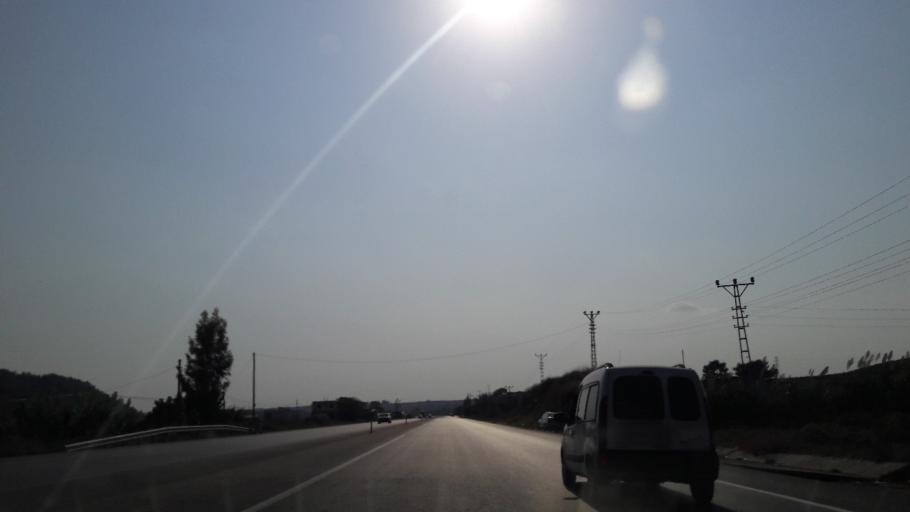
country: TR
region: Adana
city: Yuregir
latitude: 37.0688
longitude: 35.4538
